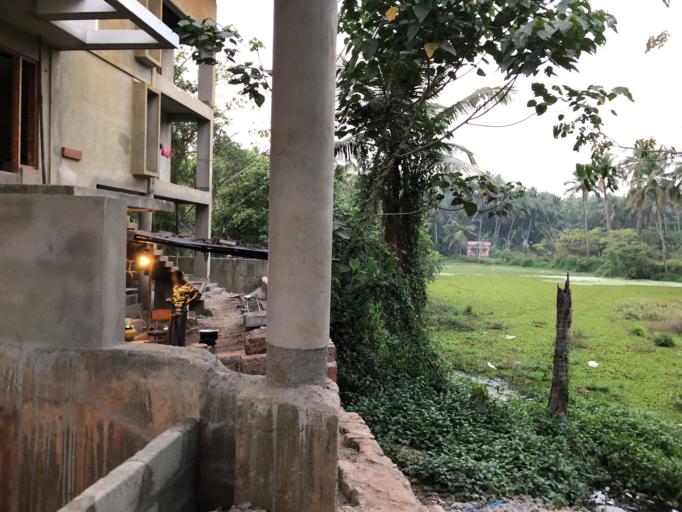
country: IN
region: Karnataka
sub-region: Dakshina Kannada
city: Mangalore
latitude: 12.8915
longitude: 74.8643
